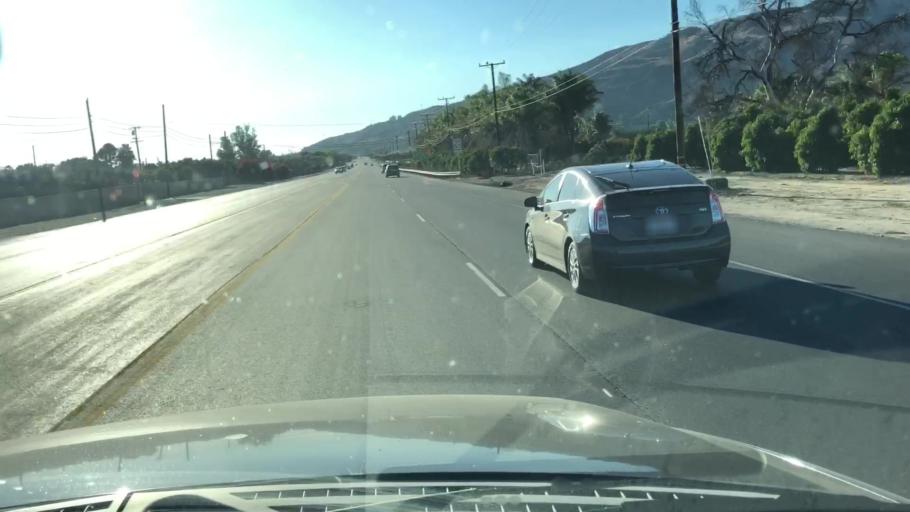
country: US
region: California
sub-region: Ventura County
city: Piru
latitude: 34.4007
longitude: -118.8128
